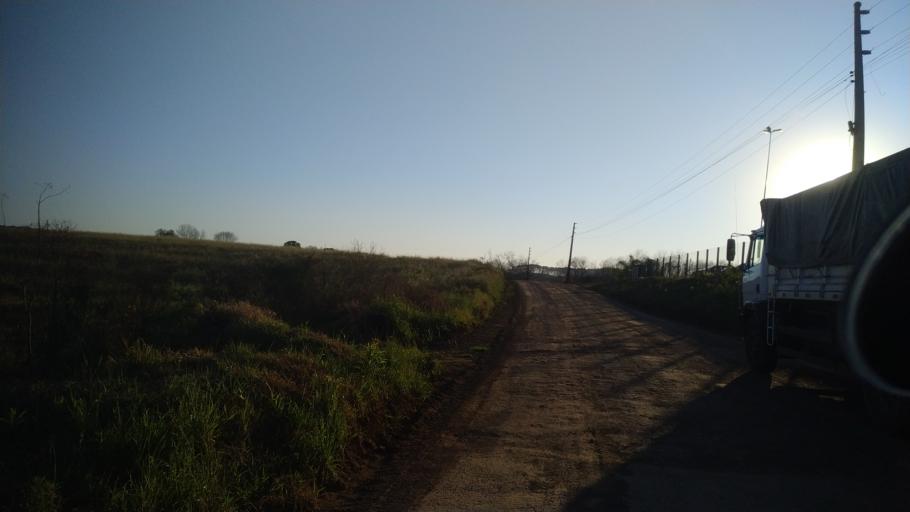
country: BR
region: Santa Catarina
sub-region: Chapeco
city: Chapeco
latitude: -27.0362
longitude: -52.6273
